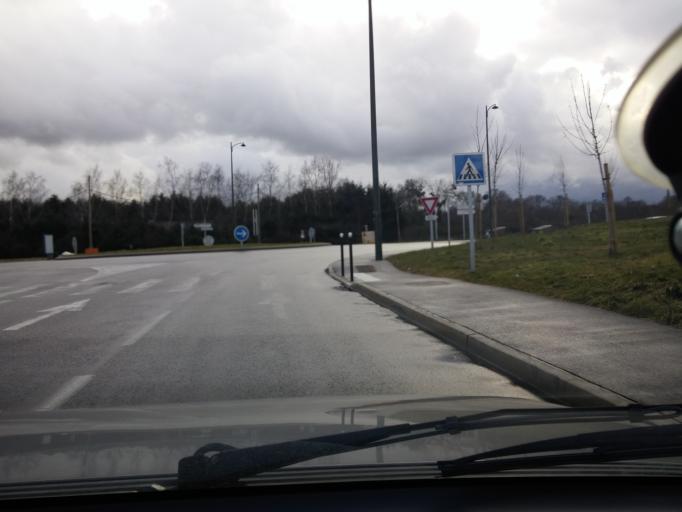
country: FR
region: Ile-de-France
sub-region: Departement du Val-de-Marne
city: La Queue-en-Brie
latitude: 48.7754
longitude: 2.5928
